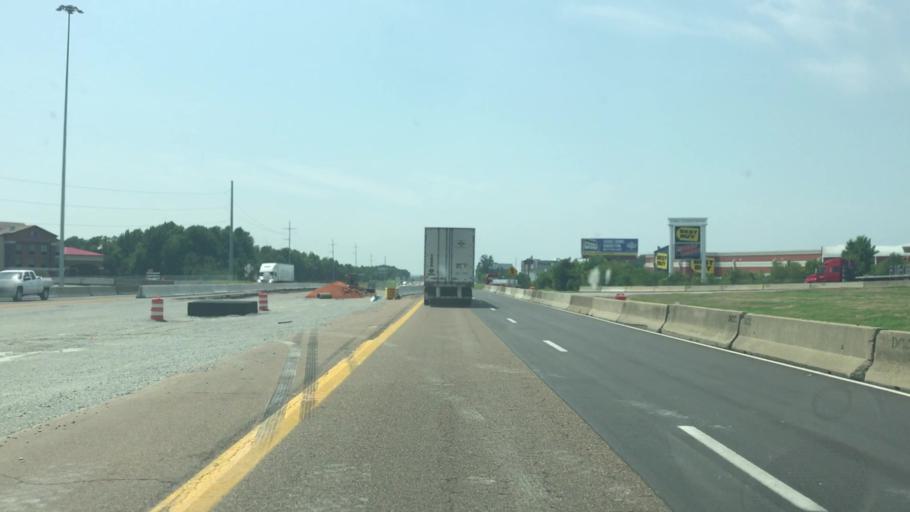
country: US
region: Tennessee
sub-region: Madison County
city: Jackson
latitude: 35.6634
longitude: -88.8554
